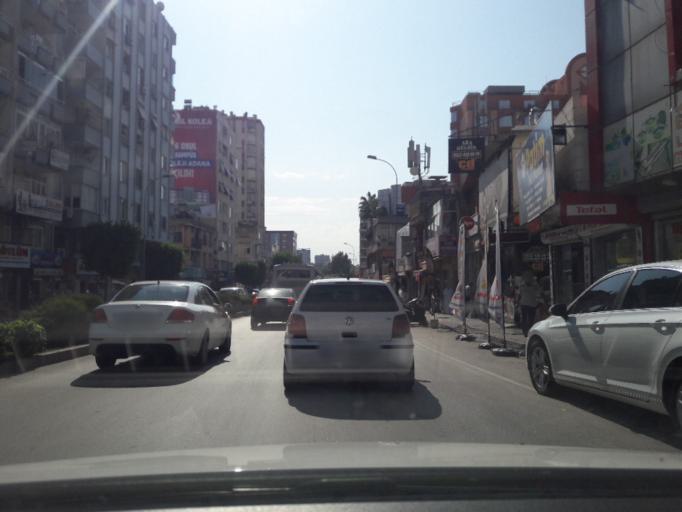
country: TR
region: Adana
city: Adana
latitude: 37.0090
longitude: 35.3239
